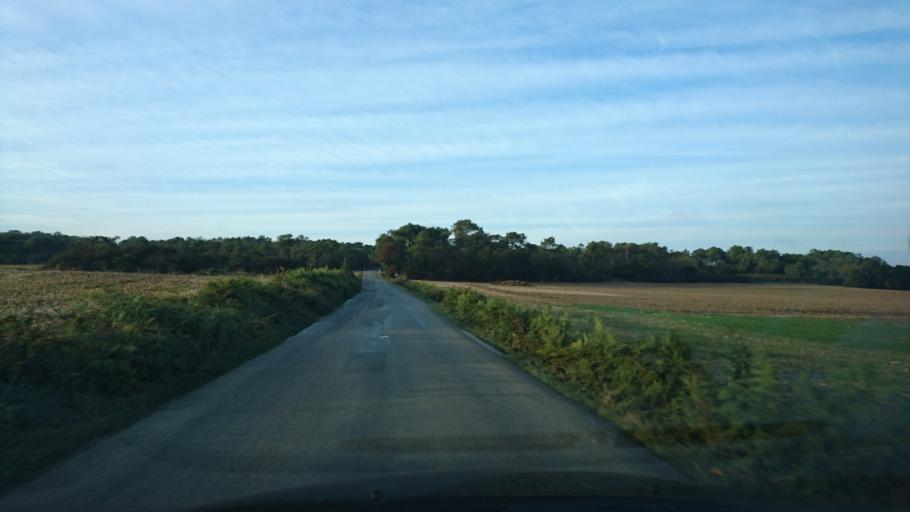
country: FR
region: Brittany
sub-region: Departement d'Ille-et-Vilaine
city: Sixt-sur-Aff
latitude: 47.7527
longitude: -2.0612
